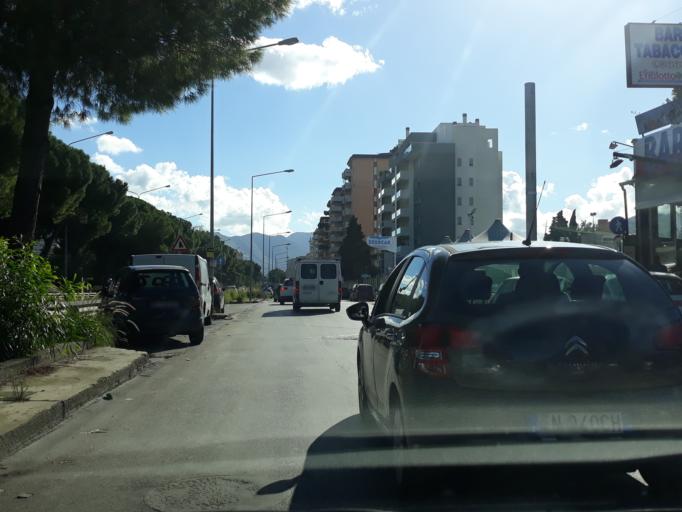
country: IT
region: Sicily
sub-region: Palermo
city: Palermo
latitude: 38.1358
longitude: 13.3305
